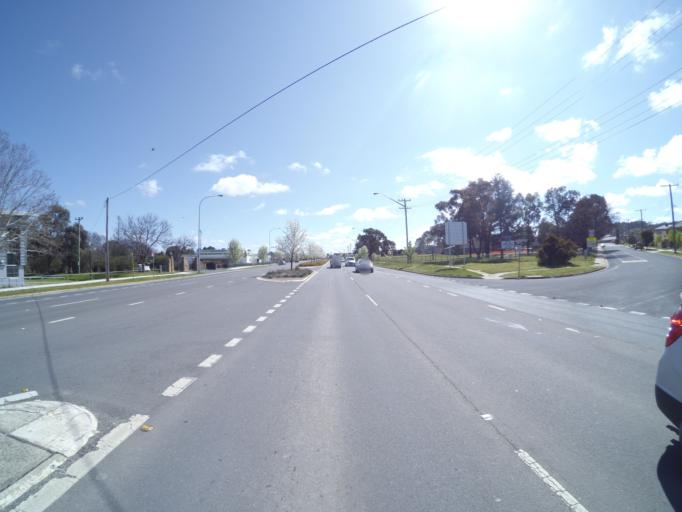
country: AU
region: New South Wales
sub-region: Queanbeyan
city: Queanbeyan
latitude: -35.3466
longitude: 149.2450
